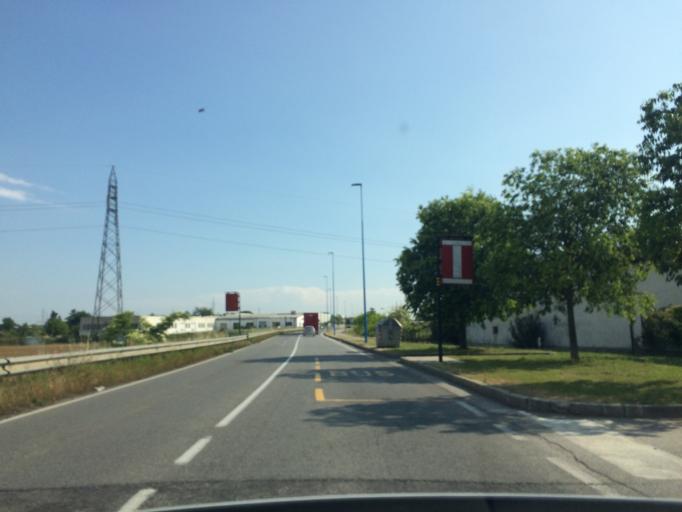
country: IT
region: Lombardy
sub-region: Provincia di Brescia
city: Folzano
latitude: 45.5068
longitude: 10.2146
